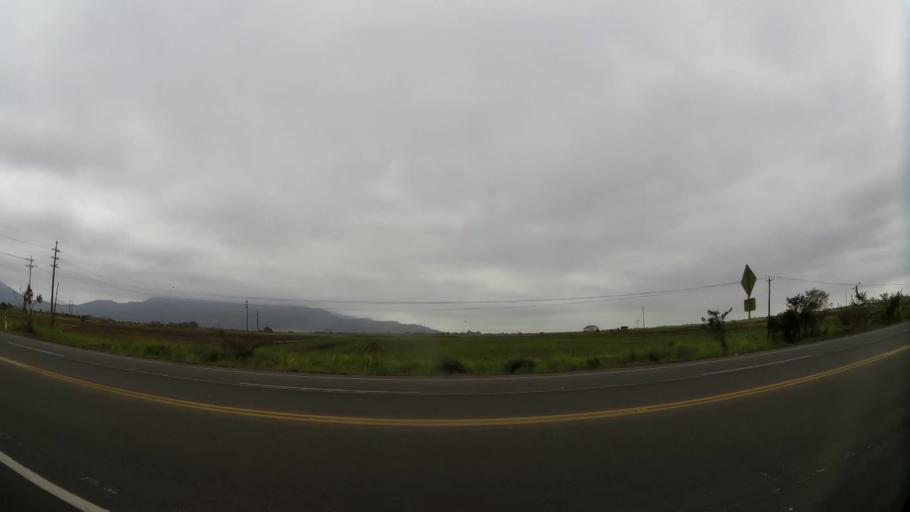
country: EC
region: Guayas
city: Naranjal
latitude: -2.5028
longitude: -79.5924
